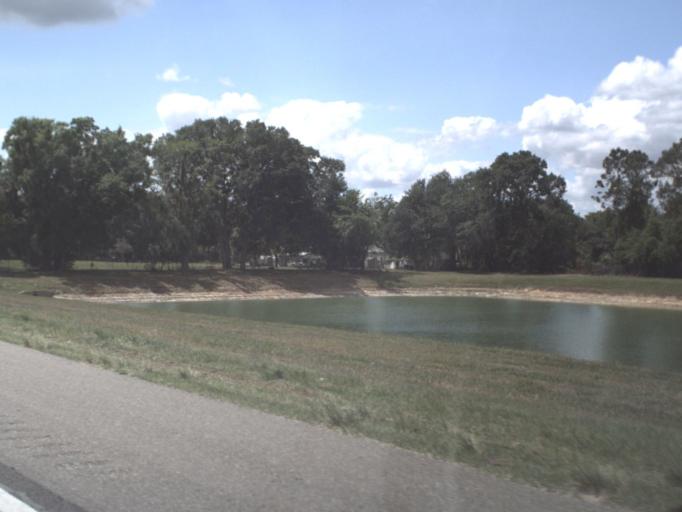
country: US
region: Florida
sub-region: Orange County
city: Ocoee
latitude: 28.5903
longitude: -81.5578
